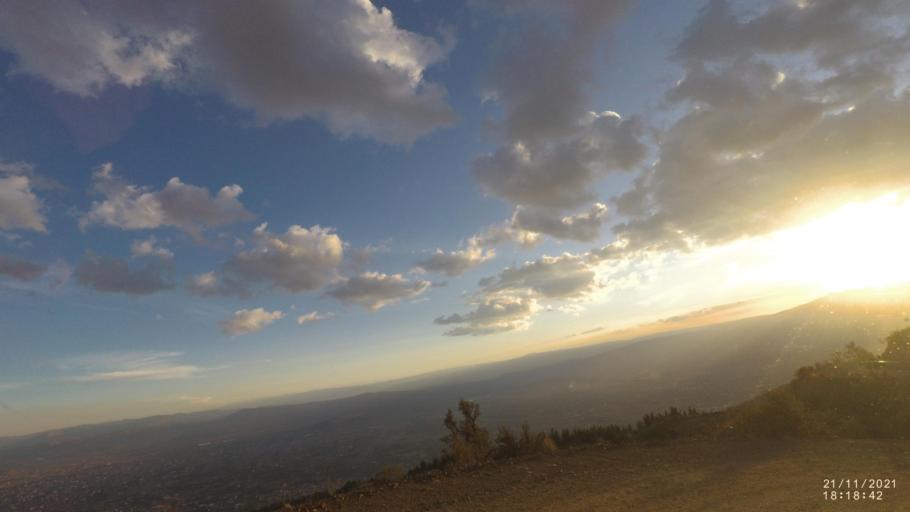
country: BO
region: Cochabamba
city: Cochabamba
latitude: -17.2919
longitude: -66.2173
